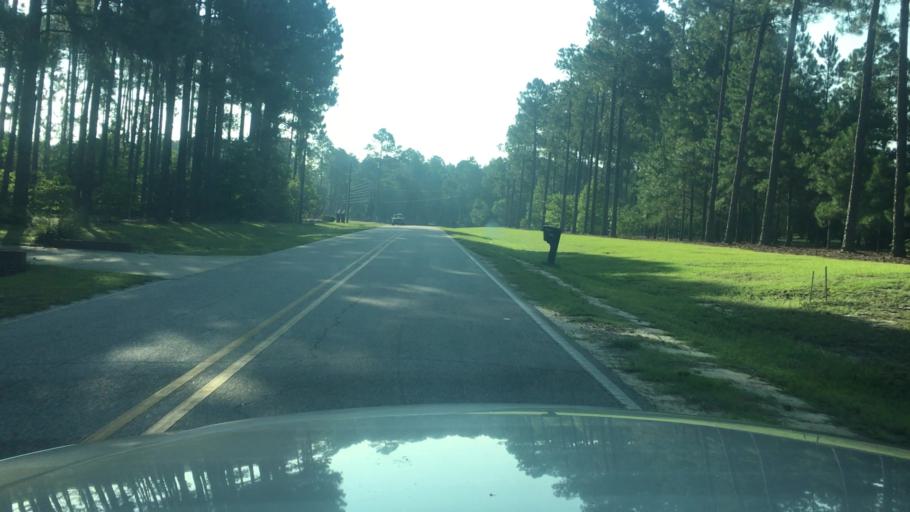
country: US
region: North Carolina
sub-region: Cumberland County
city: Spring Lake
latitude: 35.2067
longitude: -78.8901
